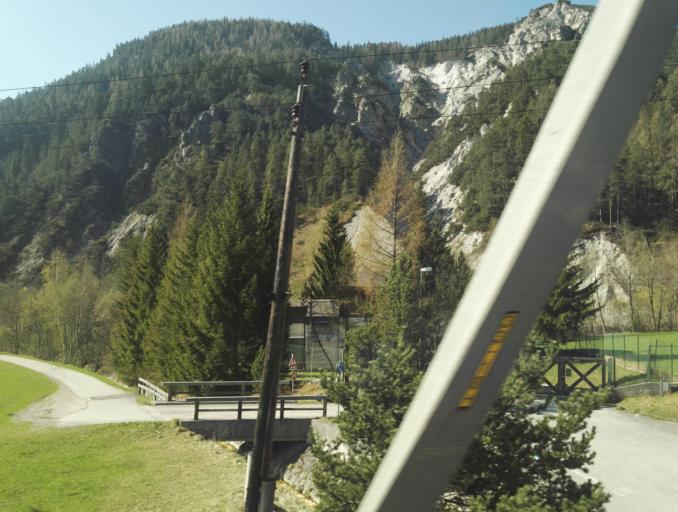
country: AT
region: Salzburg
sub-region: Politischer Bezirk Sankt Johann im Pongau
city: Forstau
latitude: 47.4003
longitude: 13.5825
